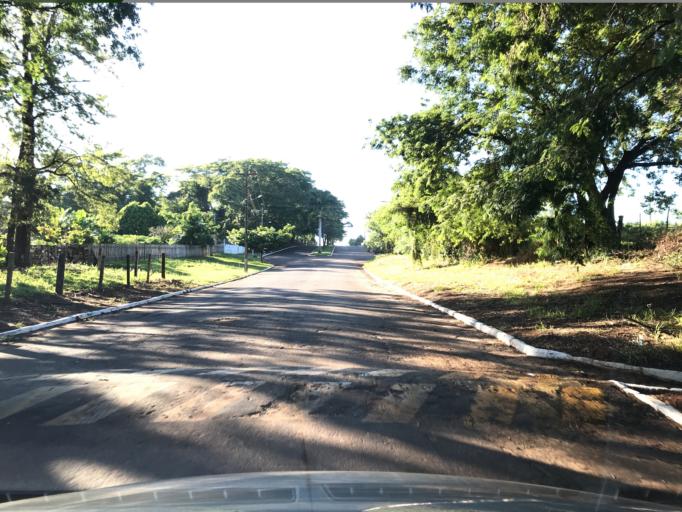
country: BR
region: Parana
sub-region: Ipora
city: Ipora
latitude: -23.9993
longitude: -53.7190
